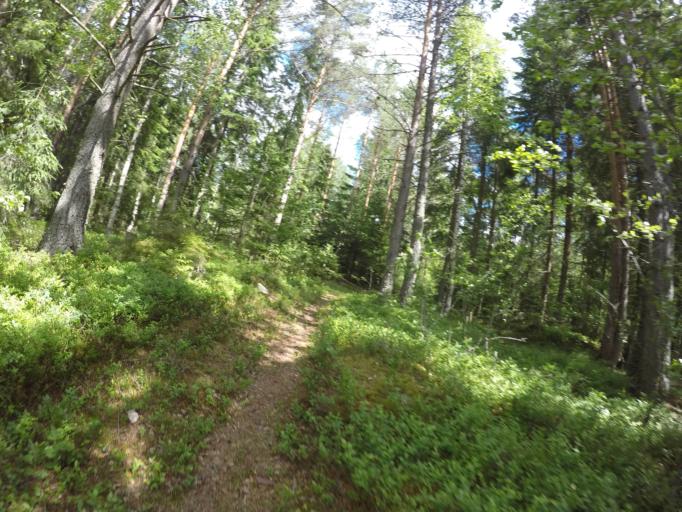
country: SE
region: Vaermland
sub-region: Filipstads Kommun
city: Lesjofors
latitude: 60.1369
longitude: 14.3005
